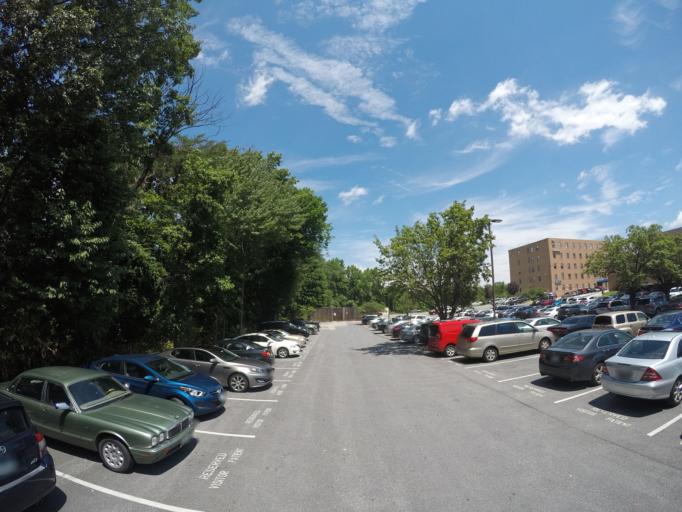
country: US
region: Maryland
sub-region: Prince George's County
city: Goddard
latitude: 38.9825
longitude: -76.8664
